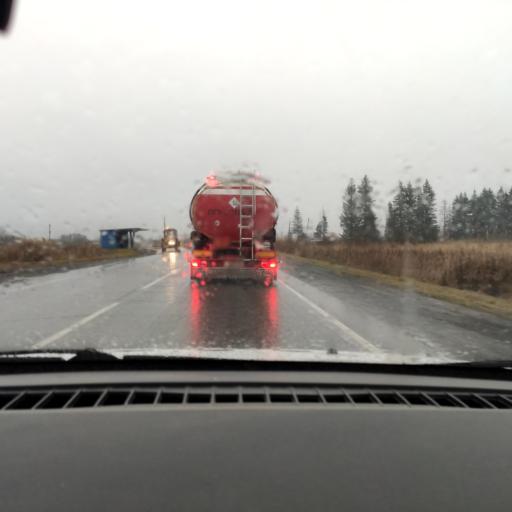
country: RU
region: Perm
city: Froly
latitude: 57.8956
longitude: 56.2599
